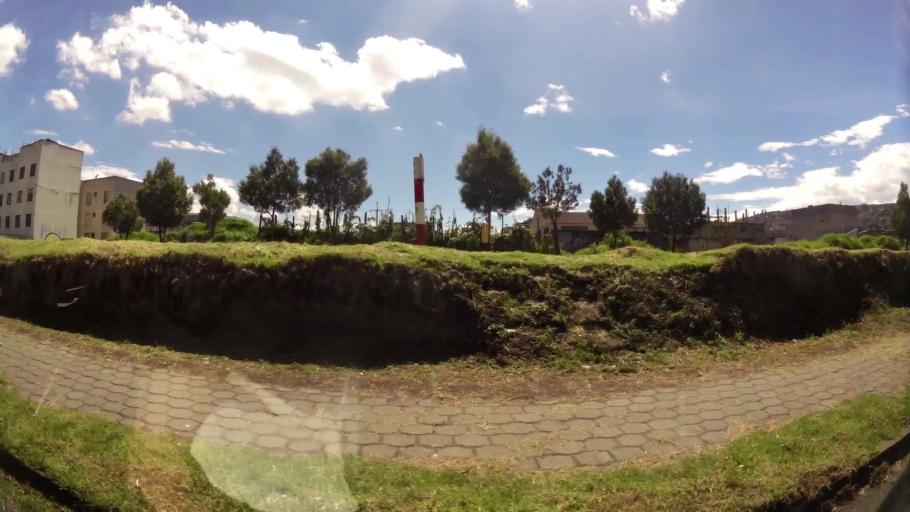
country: EC
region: Pichincha
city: Quito
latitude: -0.2918
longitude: -78.5448
